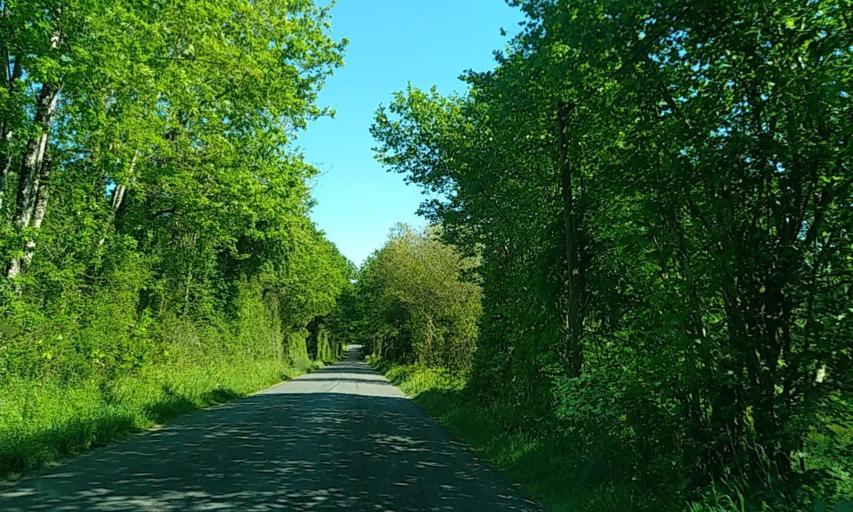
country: FR
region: Poitou-Charentes
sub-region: Departement des Deux-Sevres
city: Boisme
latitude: 46.7830
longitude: -0.4491
